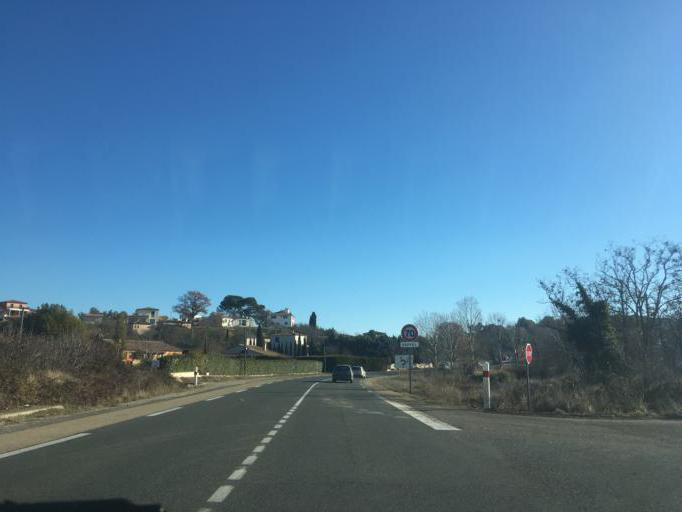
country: FR
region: Provence-Alpes-Cote d'Azur
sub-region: Departement du Var
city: Draguignan
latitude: 43.5277
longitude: 6.4339
